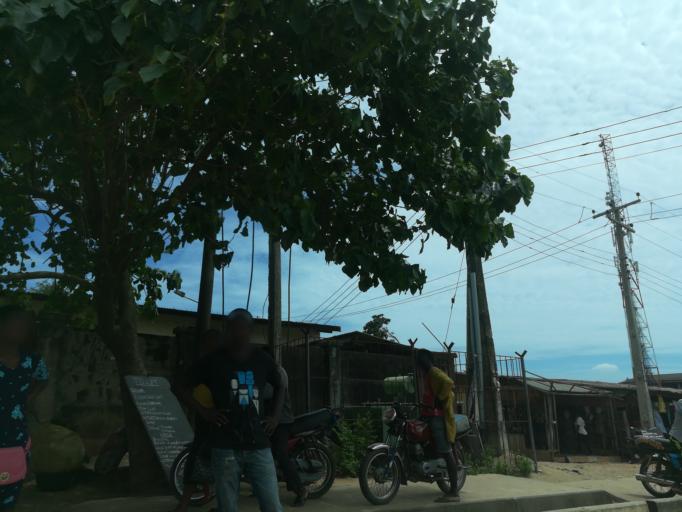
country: NG
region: Lagos
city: Ebute Ikorodu
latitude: 6.5699
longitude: 3.4819
